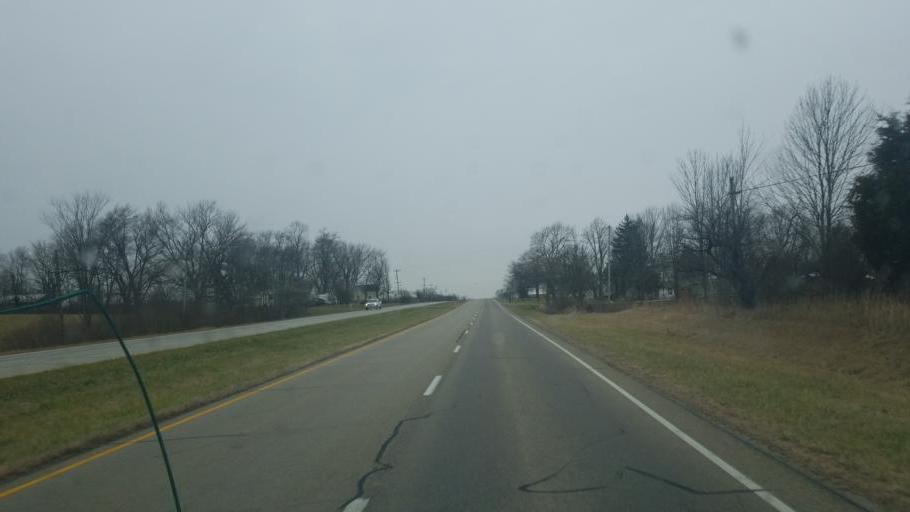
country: US
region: Indiana
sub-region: Henry County
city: Knightstown
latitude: 39.7939
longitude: -85.5491
